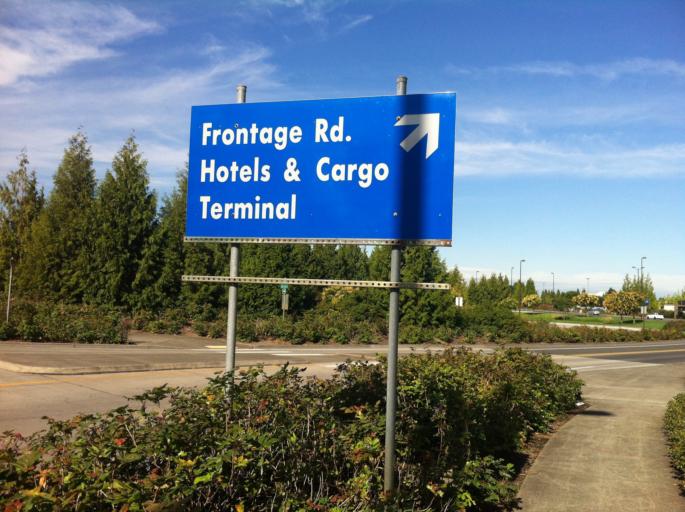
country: US
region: Washington
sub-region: Clark County
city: Orchards
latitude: 45.5779
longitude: -122.5596
